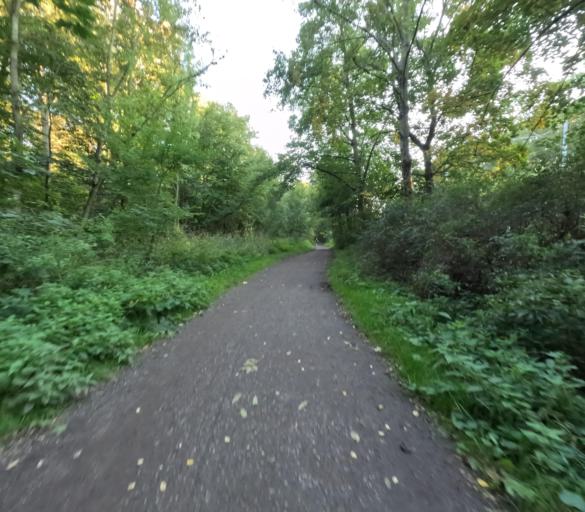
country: DE
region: Saxony
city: Leipzig
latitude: 51.3618
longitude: 12.3232
